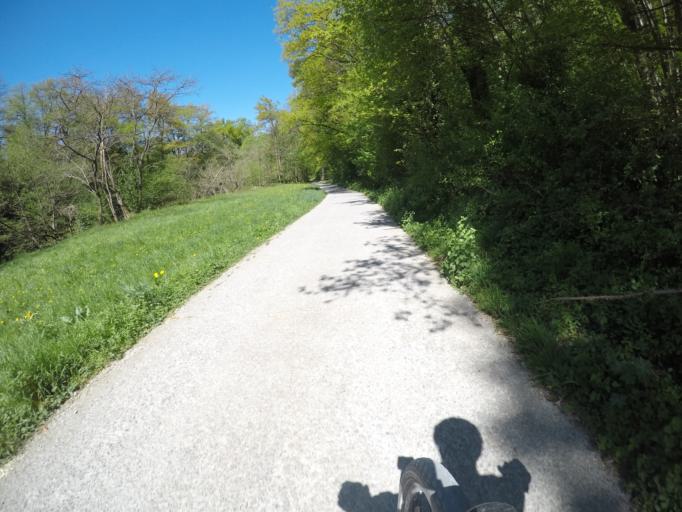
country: DE
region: Baden-Wuerttemberg
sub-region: Regierungsbezirk Stuttgart
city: Waiblingen
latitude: 48.8670
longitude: 9.3065
